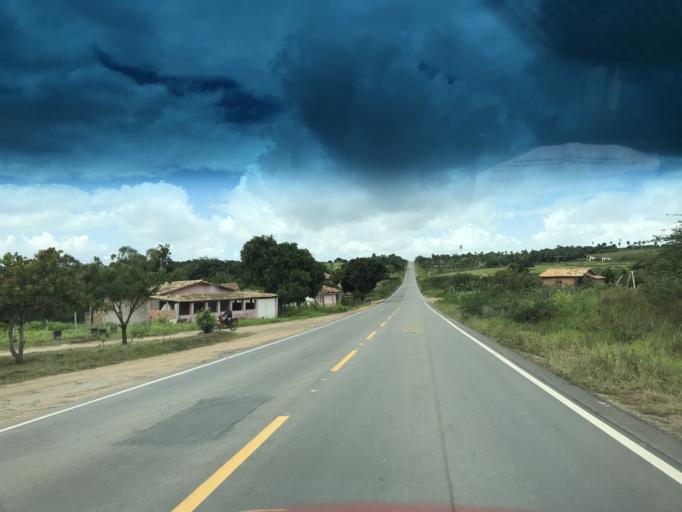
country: BR
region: Bahia
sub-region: Conceicao Do Almeida
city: Conceicao do Almeida
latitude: -12.6867
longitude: -39.2509
